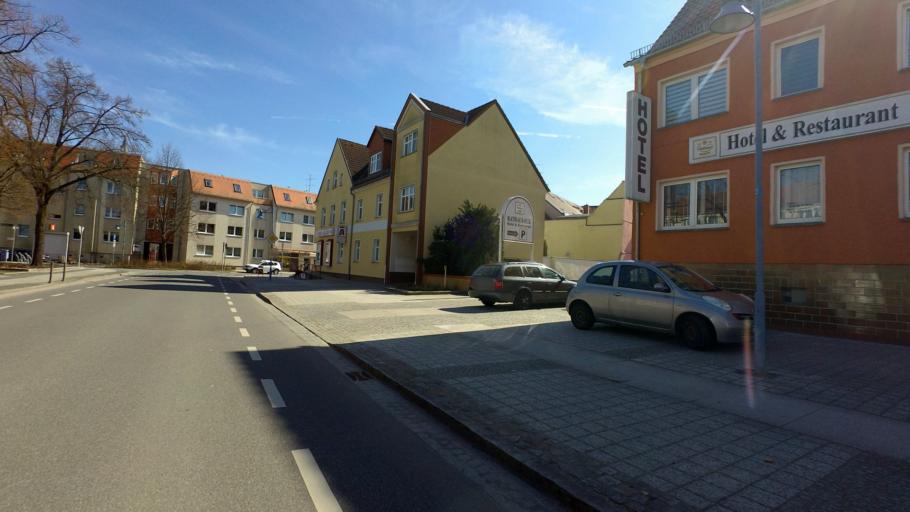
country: DE
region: Brandenburg
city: Muncheberg
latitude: 52.5035
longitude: 14.1399
